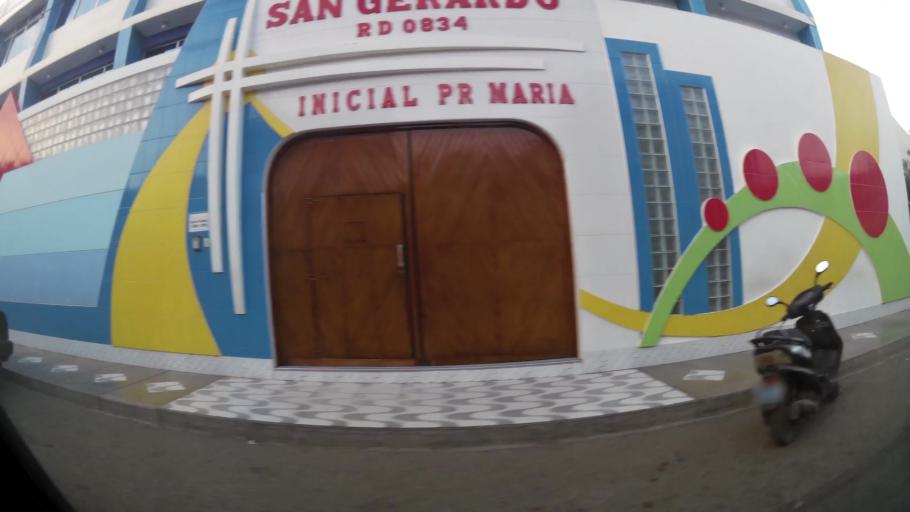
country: PE
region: La Libertad
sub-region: Provincia de Trujillo
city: Trujillo
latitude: -8.1011
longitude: -79.0380
